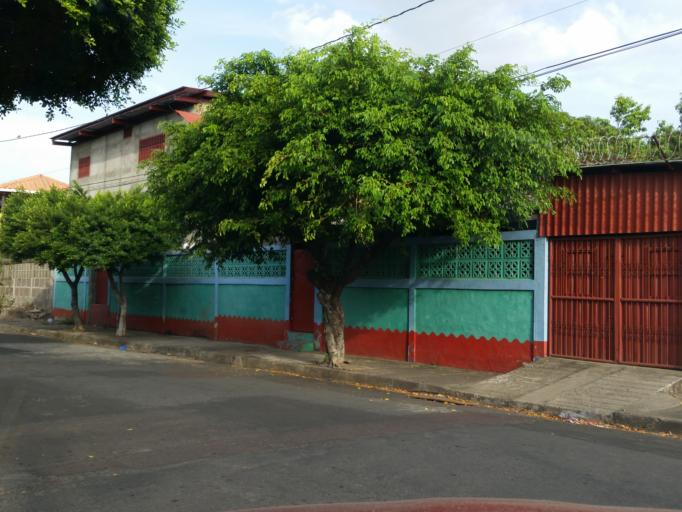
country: NI
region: Managua
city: Managua
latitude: 12.1448
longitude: -86.2804
